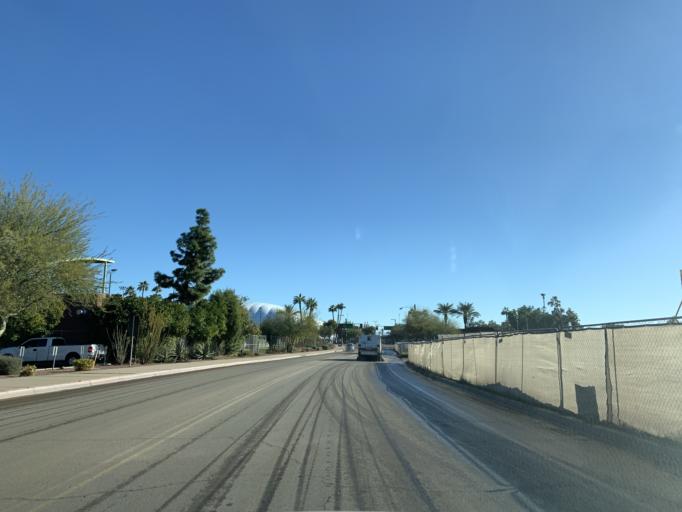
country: US
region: Arizona
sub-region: Maricopa County
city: Tempe Junction
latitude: 33.4245
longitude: -111.9282
